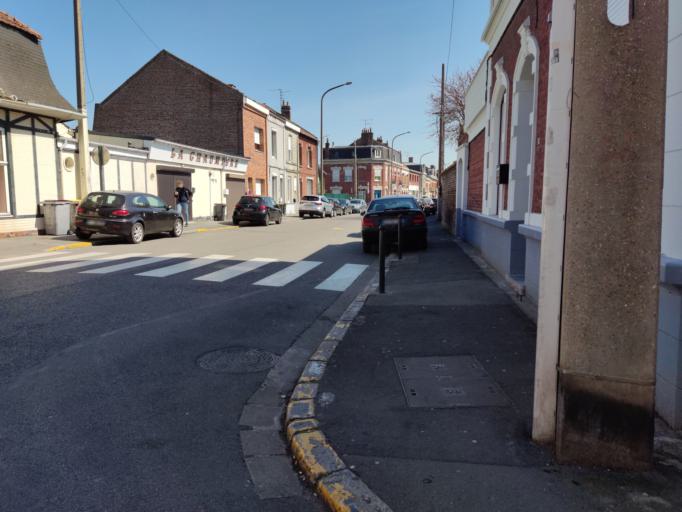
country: FR
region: Nord-Pas-de-Calais
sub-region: Departement du Pas-de-Calais
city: Montigny-en-Gohelle
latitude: 50.4192
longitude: 2.9498
